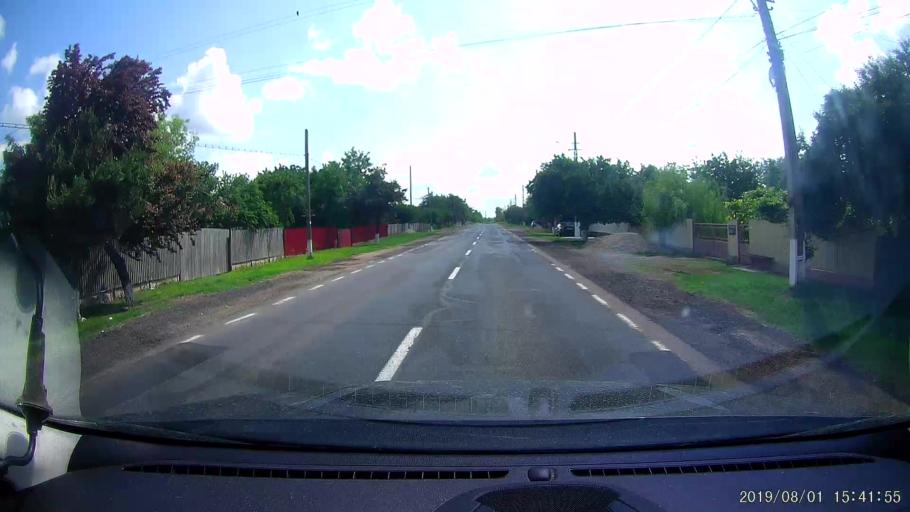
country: RO
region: Braila
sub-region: Comuna Baraganul
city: Baraganul
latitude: 44.8173
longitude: 27.5202
